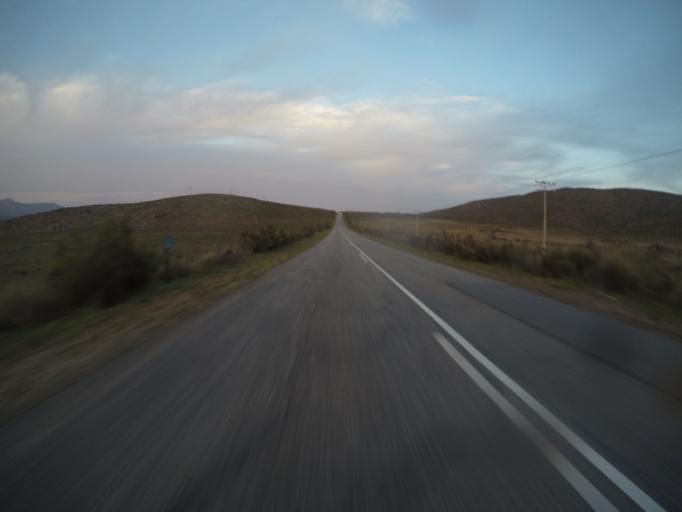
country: ZA
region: Western Cape
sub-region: Eden District Municipality
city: Plettenberg Bay
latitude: -33.7428
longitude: 23.4458
